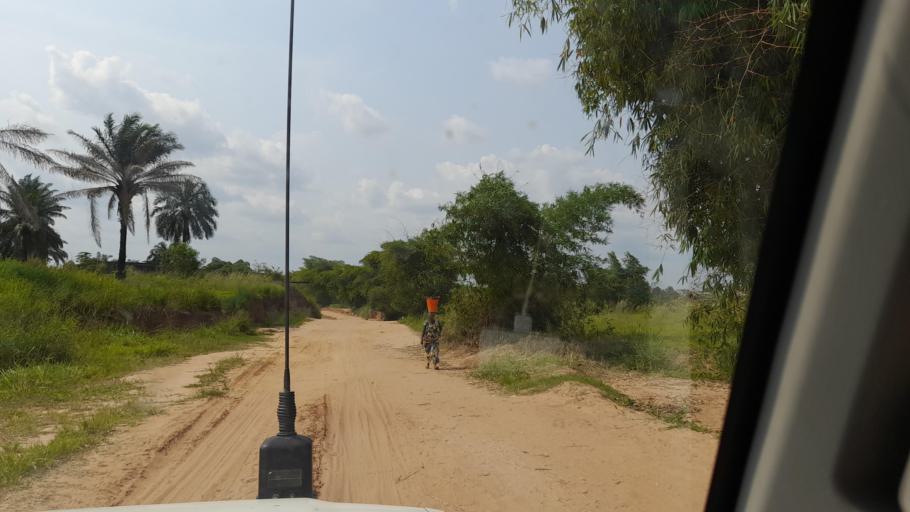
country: CD
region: Kasai-Occidental
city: Kananga
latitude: -5.9132
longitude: 22.4772
